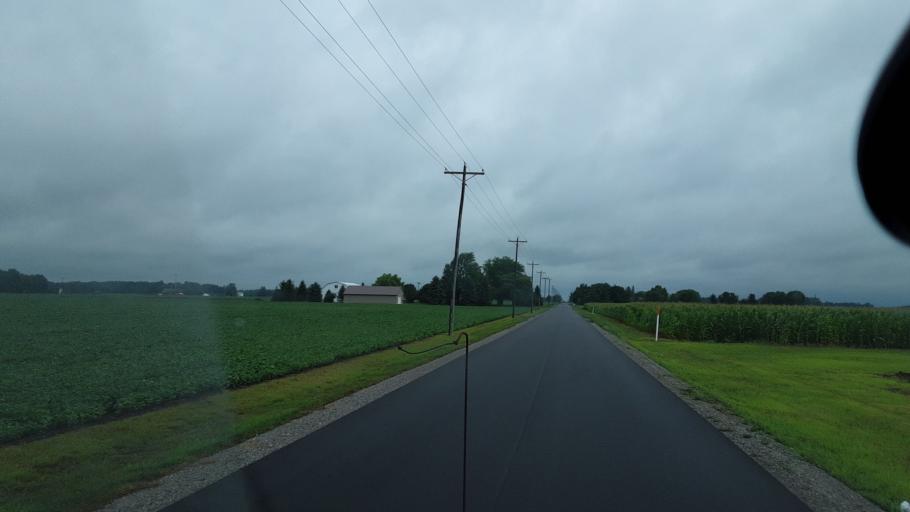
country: US
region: Indiana
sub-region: Adams County
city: Decatur
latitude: 40.8456
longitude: -84.8427
